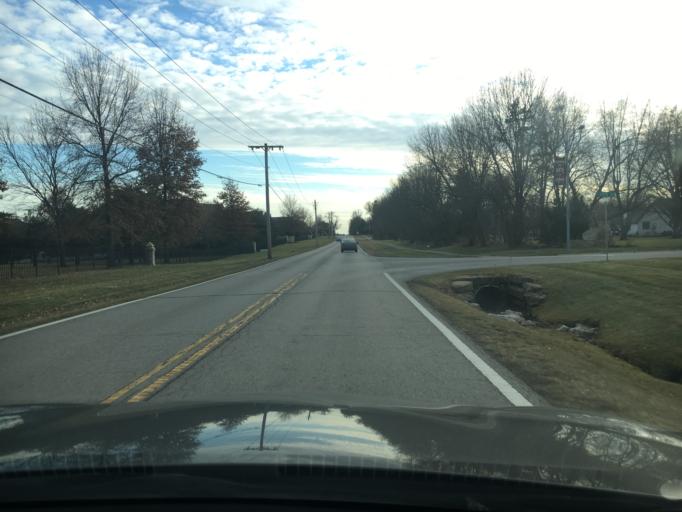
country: US
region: Kansas
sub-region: Johnson County
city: Leawood
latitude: 38.8788
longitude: -94.6306
